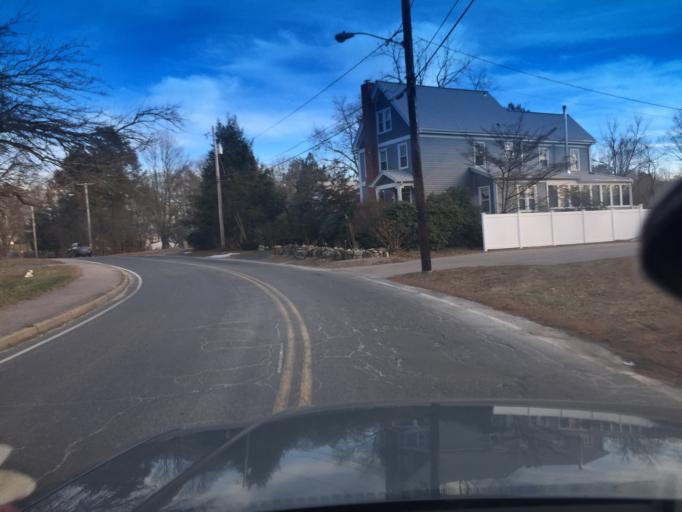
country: US
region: Massachusetts
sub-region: Middlesex County
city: Holliston
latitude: 42.1986
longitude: -71.4228
